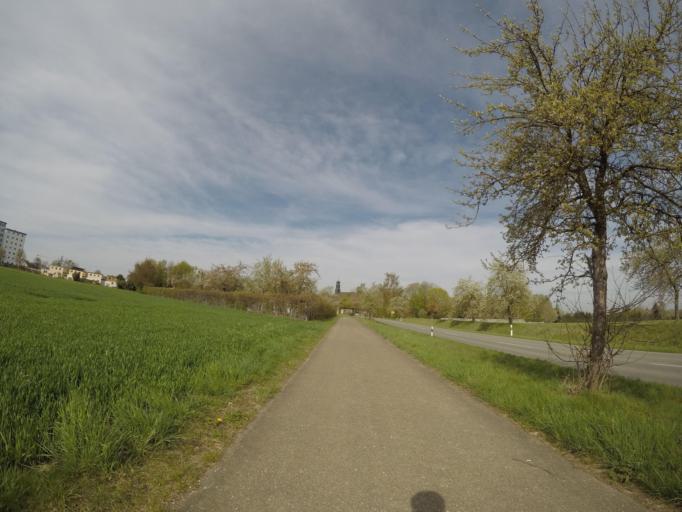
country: DE
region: Baden-Wuerttemberg
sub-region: Tuebingen Region
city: Saulgau
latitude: 48.0143
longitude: 9.5135
